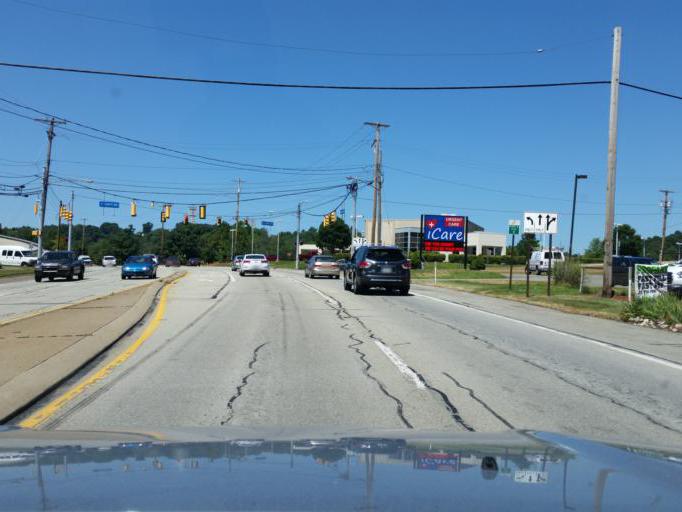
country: US
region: Pennsylvania
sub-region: Westmoreland County
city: Murrysville
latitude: 40.4303
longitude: -79.7101
